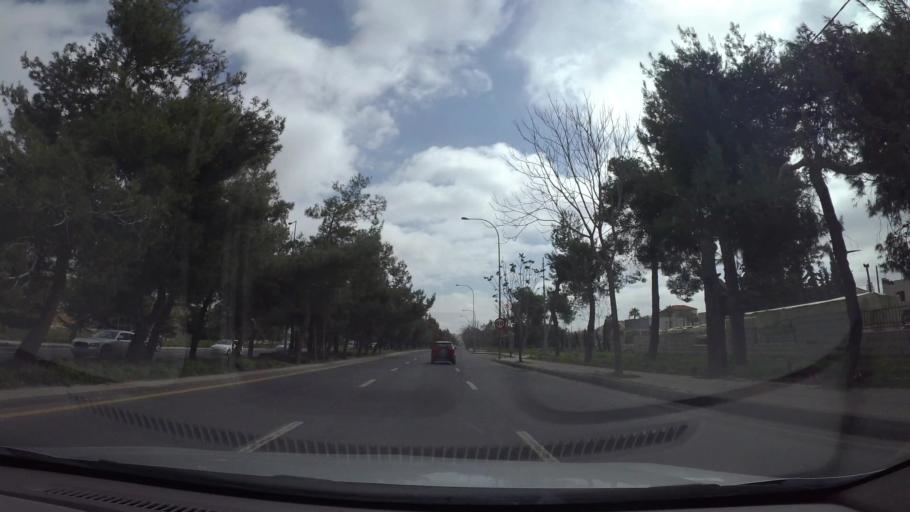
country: JO
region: Amman
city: Wadi as Sir
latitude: 31.9939
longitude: 35.8193
